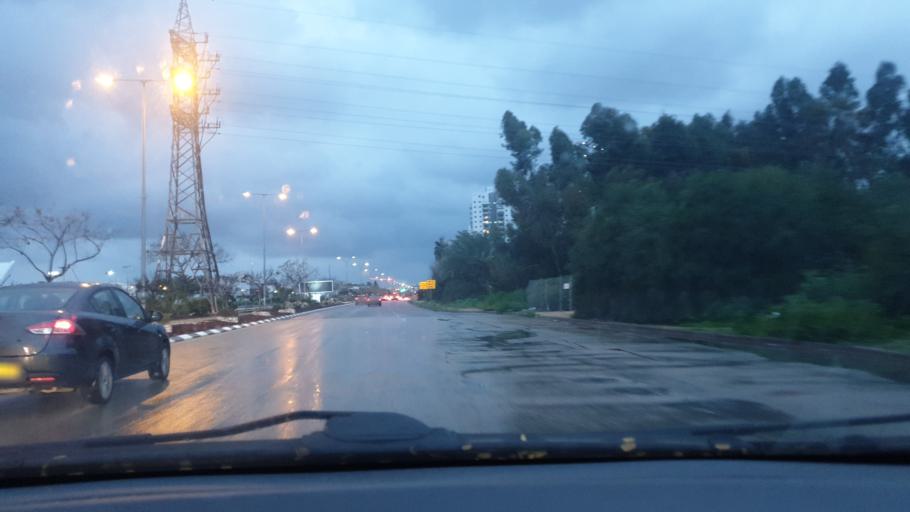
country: IL
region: Central District
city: Rishon LeZiyyon
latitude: 31.9829
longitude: 34.8002
